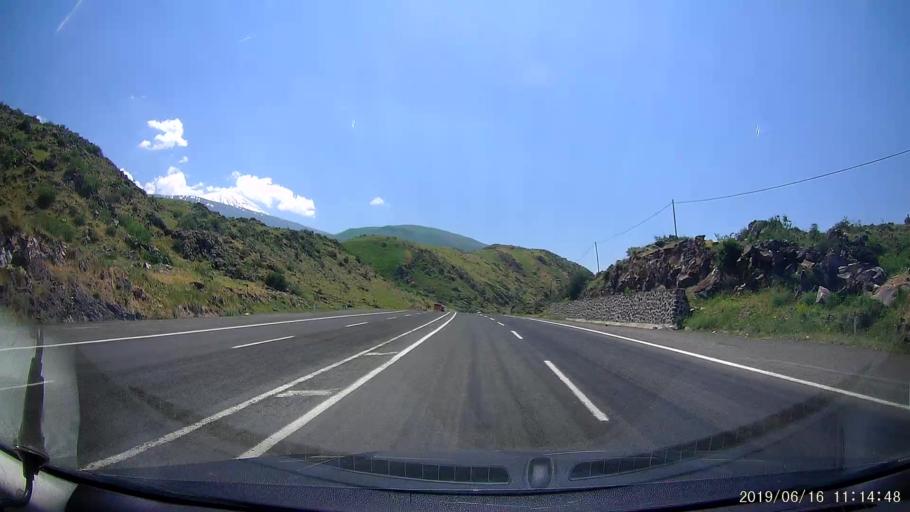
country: TR
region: Igdir
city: Igdir
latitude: 39.7731
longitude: 44.1419
